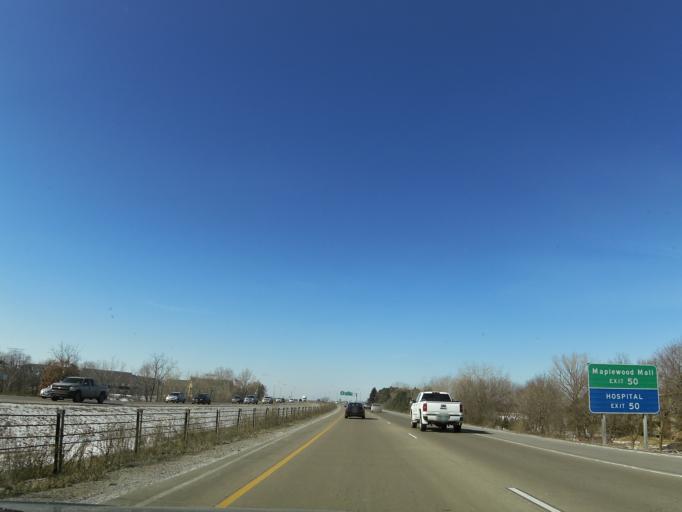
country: US
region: Minnesota
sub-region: Ramsey County
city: North Saint Paul
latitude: 45.0371
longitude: -93.0084
